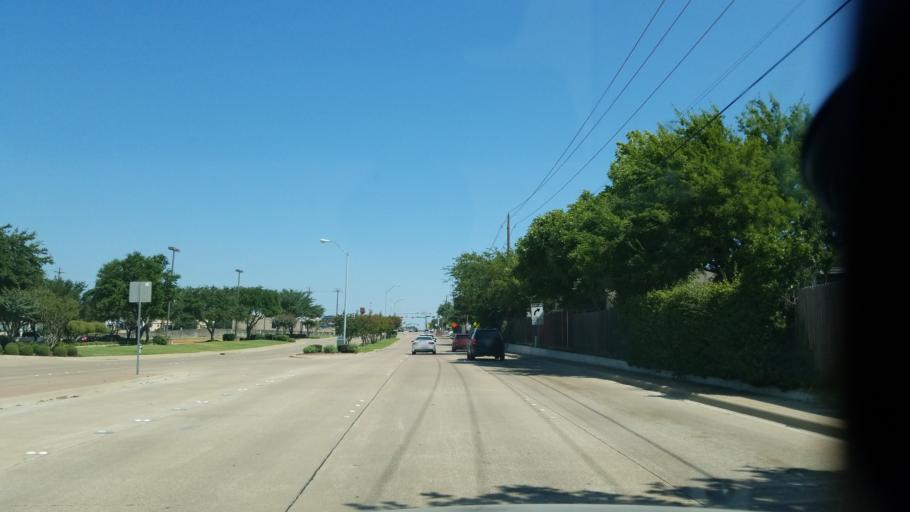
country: US
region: Texas
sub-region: Dallas County
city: Duncanville
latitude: 32.6380
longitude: -96.8913
